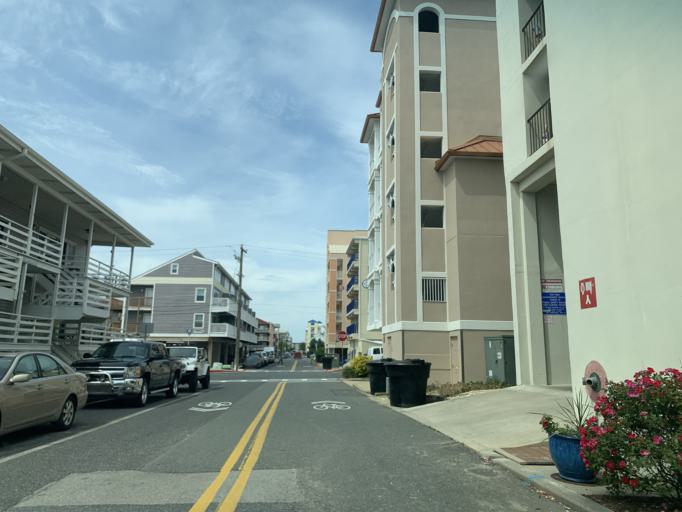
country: US
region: Delaware
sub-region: Sussex County
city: Bethany Beach
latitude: 38.4438
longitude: -75.0511
